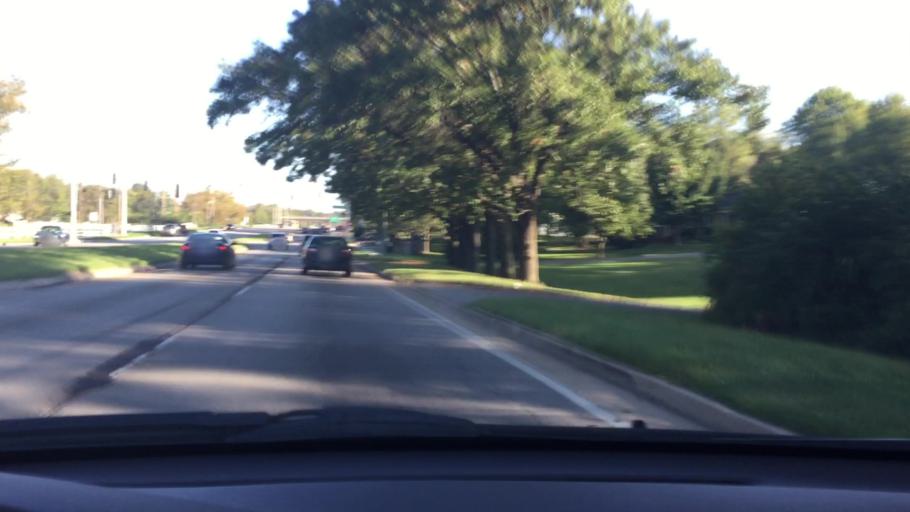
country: US
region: Kentucky
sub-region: Fayette County
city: Lexington
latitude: 37.9867
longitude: -84.4941
